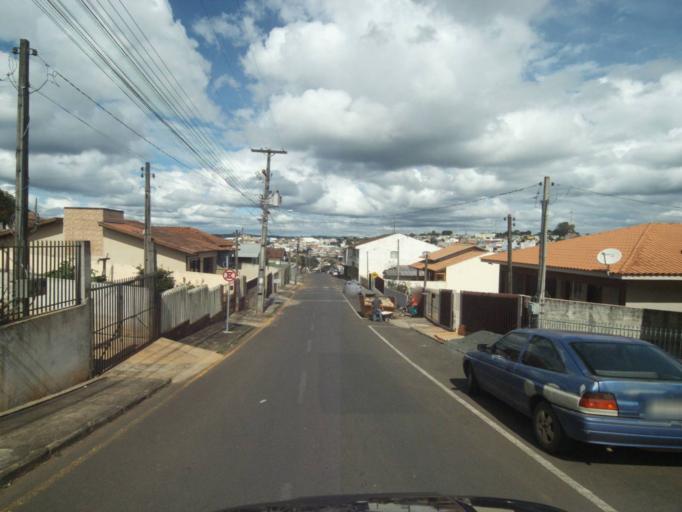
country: BR
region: Parana
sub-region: Telemaco Borba
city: Telemaco Borba
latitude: -24.3240
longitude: -50.6305
